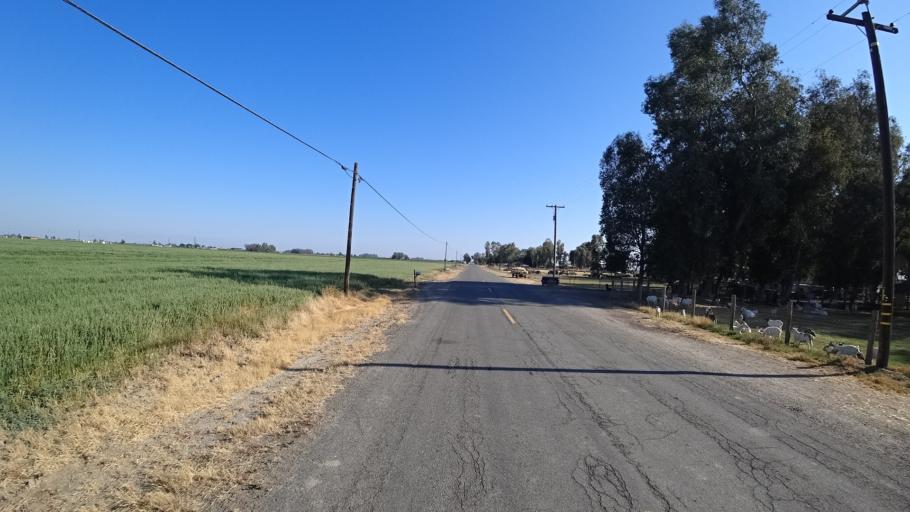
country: US
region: California
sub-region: Fresno County
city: Riverdale
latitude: 36.3489
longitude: -119.8693
